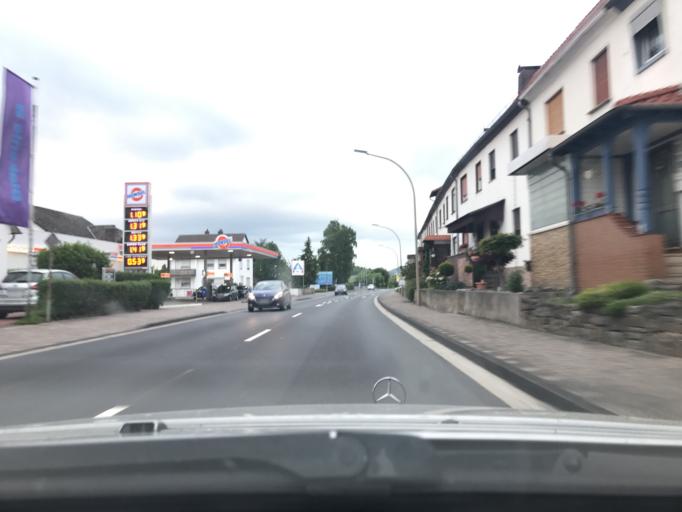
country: DE
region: Hesse
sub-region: Regierungsbezirk Kassel
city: Eschwege
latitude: 51.1569
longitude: 10.0005
